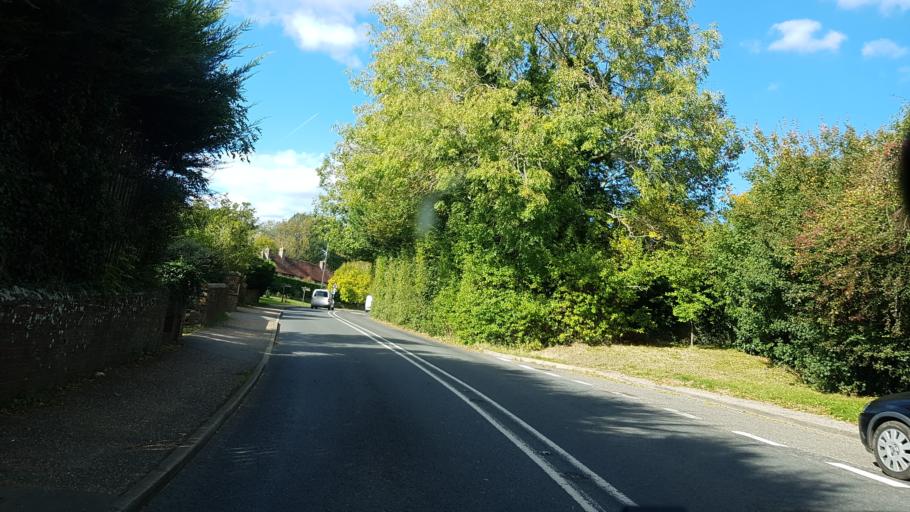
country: GB
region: England
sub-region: Surrey
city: Chiddingfold
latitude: 51.0539
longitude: -0.6436
